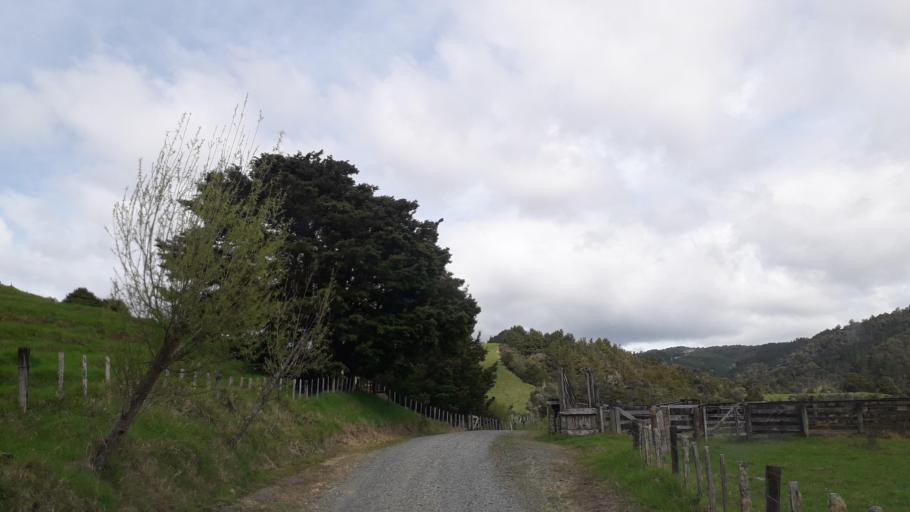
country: NZ
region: Northland
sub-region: Far North District
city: Waimate North
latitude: -35.1604
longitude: 173.7197
